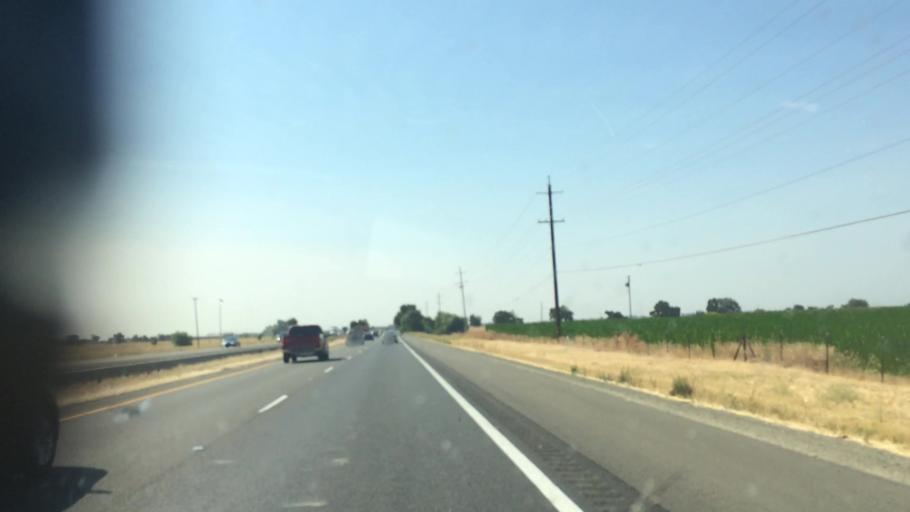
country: US
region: California
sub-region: Sacramento County
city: Elk Grove
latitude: 38.3355
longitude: -121.3321
